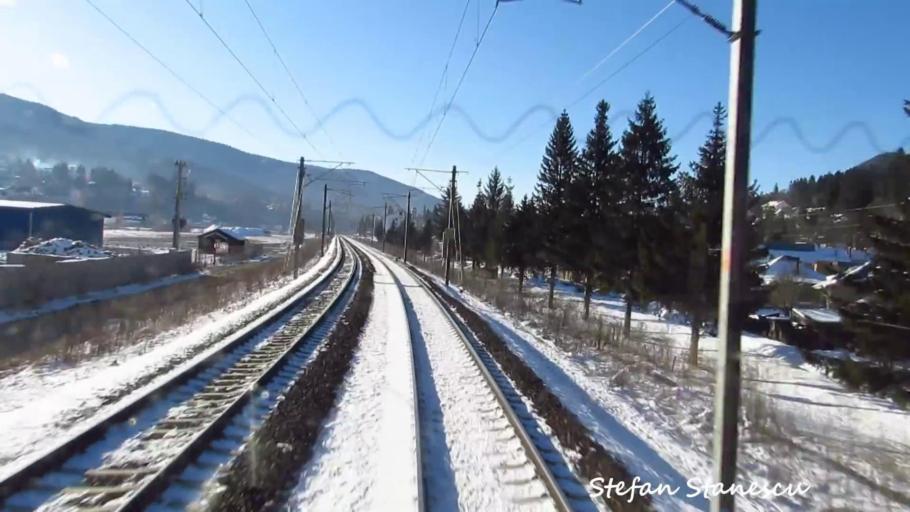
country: RO
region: Prahova
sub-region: Oras Busteni
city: Poiana Tapului
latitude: 45.3887
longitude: 25.5408
